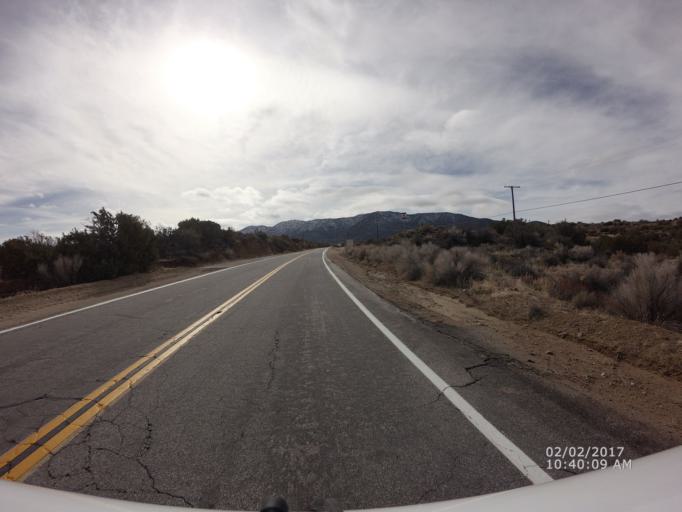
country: US
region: California
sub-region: Los Angeles County
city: Littlerock
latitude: 34.4640
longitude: -117.9350
